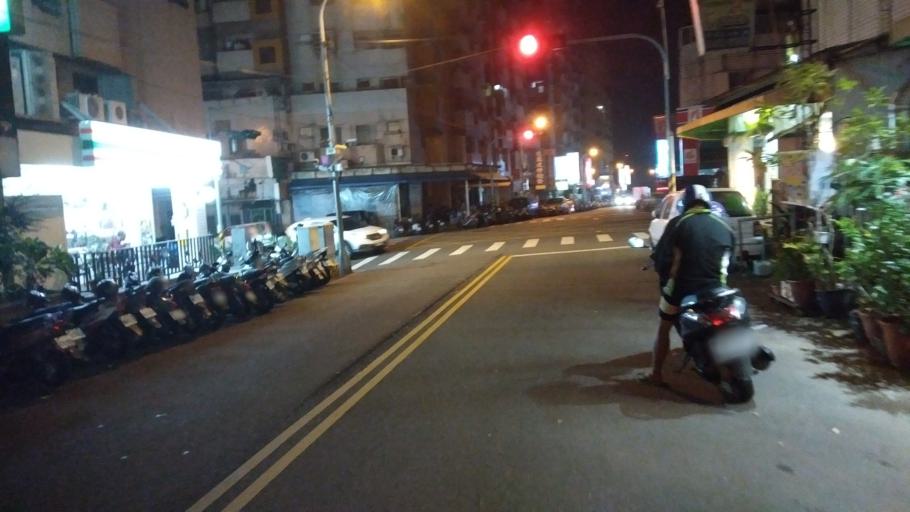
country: TW
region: Taiwan
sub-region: Taichung City
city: Taichung
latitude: 24.1863
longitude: 120.6080
